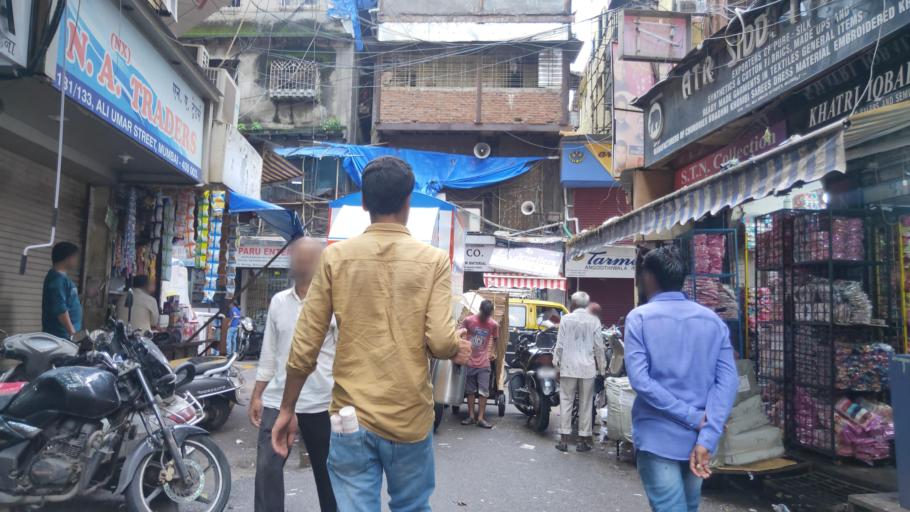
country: IN
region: Maharashtra
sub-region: Mumbai Suburban
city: Mumbai
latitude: 18.9548
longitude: 72.8310
